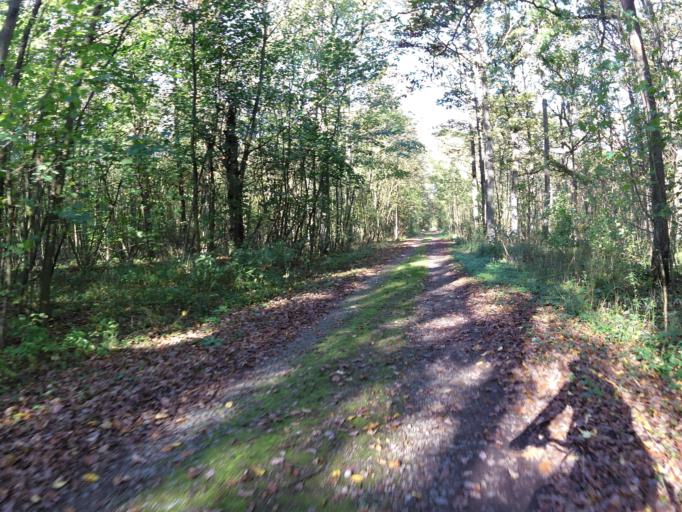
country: DE
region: Bavaria
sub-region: Regierungsbezirk Unterfranken
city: Frickenhausen
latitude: 49.7144
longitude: 10.0884
